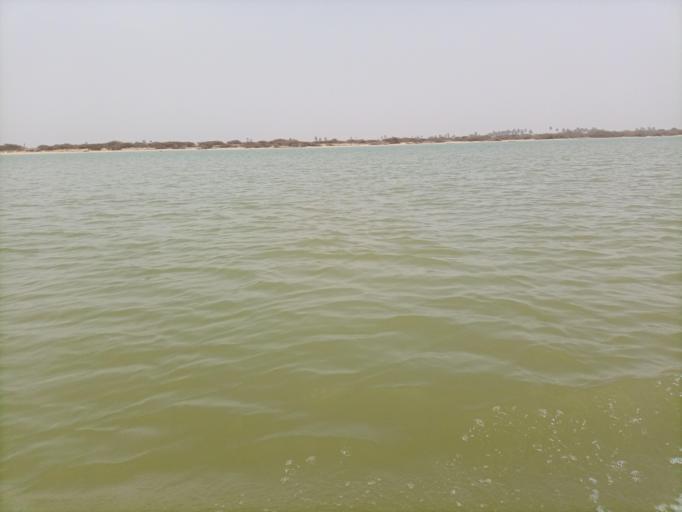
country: SN
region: Saint-Louis
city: Saint-Louis
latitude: 15.8572
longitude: -16.5171
